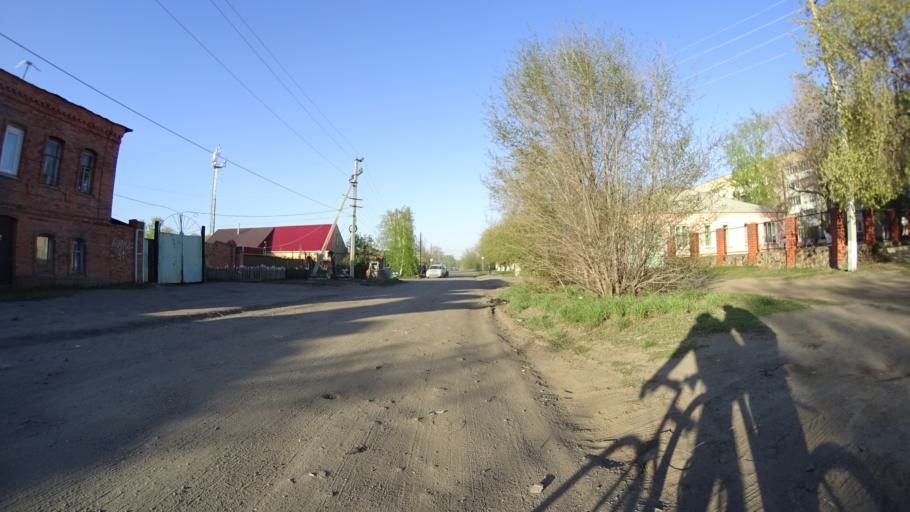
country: RU
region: Chelyabinsk
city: Troitsk
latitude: 54.0890
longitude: 61.5432
